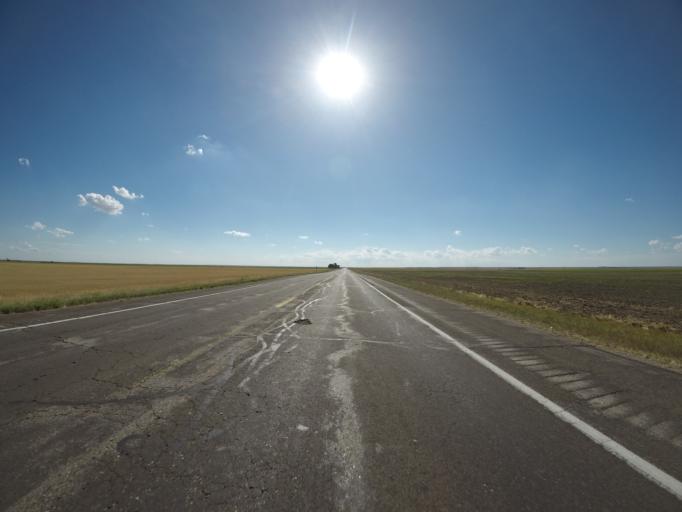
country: US
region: Colorado
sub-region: Logan County
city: Sterling
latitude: 40.6239
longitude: -103.3379
